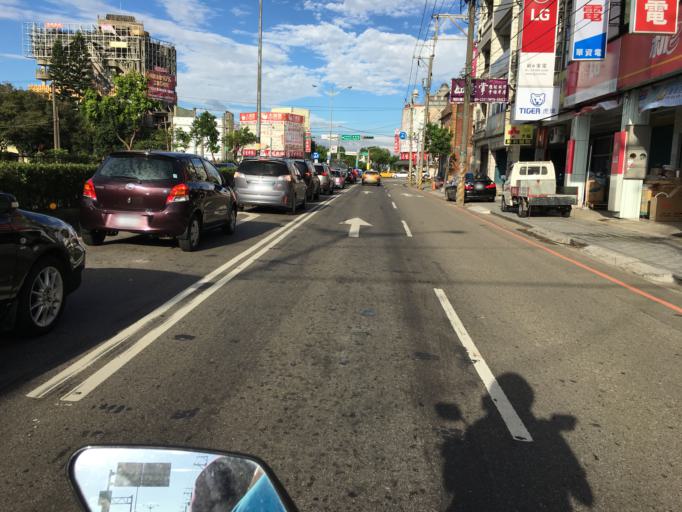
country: TW
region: Taiwan
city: Daxi
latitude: 24.8689
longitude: 121.2131
